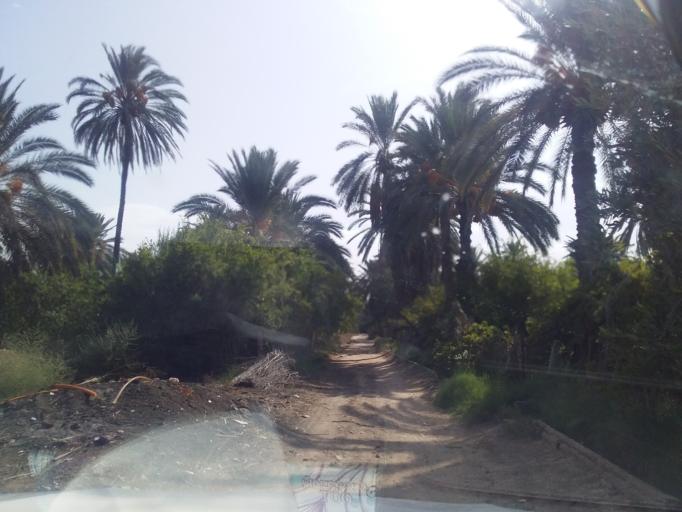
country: TN
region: Qabis
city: Gabes
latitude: 33.6278
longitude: 10.2893
